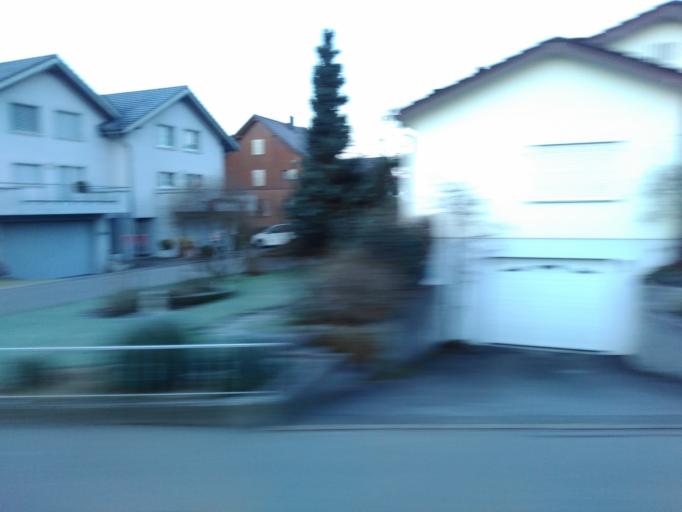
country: CH
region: Schwyz
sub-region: Bezirk March
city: Schubelbach
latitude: 47.1888
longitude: 8.8971
